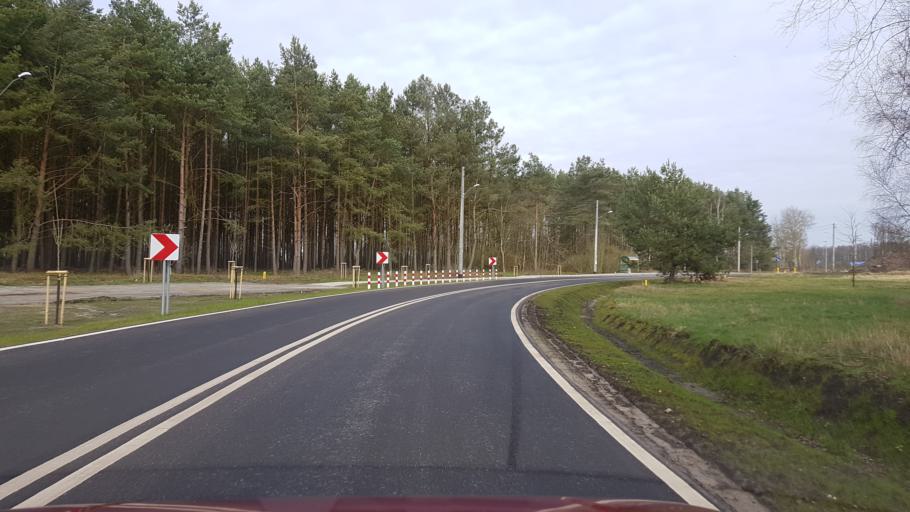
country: PL
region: West Pomeranian Voivodeship
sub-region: Powiat policki
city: Nowe Warpno
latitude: 53.6895
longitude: 14.3547
